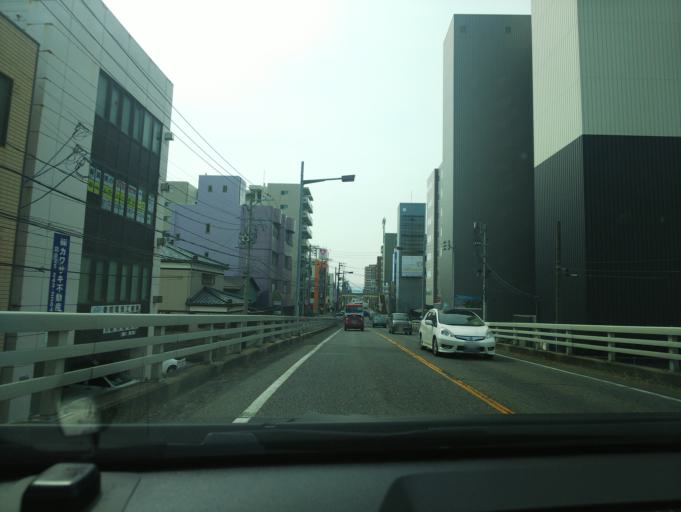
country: JP
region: Niigata
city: Niigata-shi
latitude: 37.9124
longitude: 139.0674
